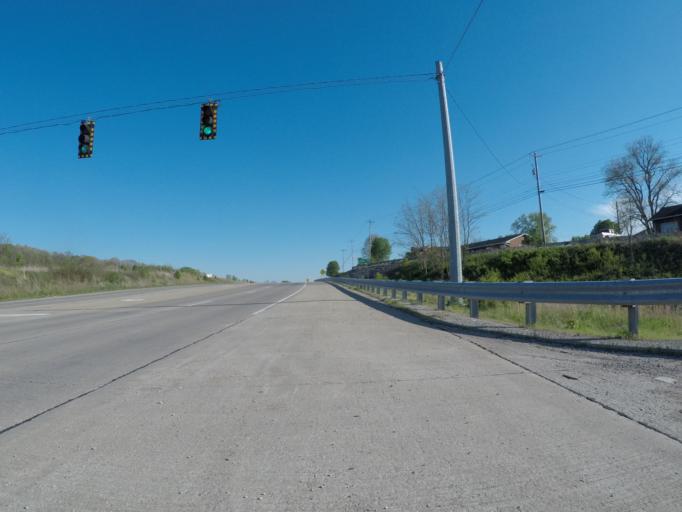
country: US
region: Kentucky
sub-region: Boyd County
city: Meads
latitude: 38.3642
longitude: -82.6989
